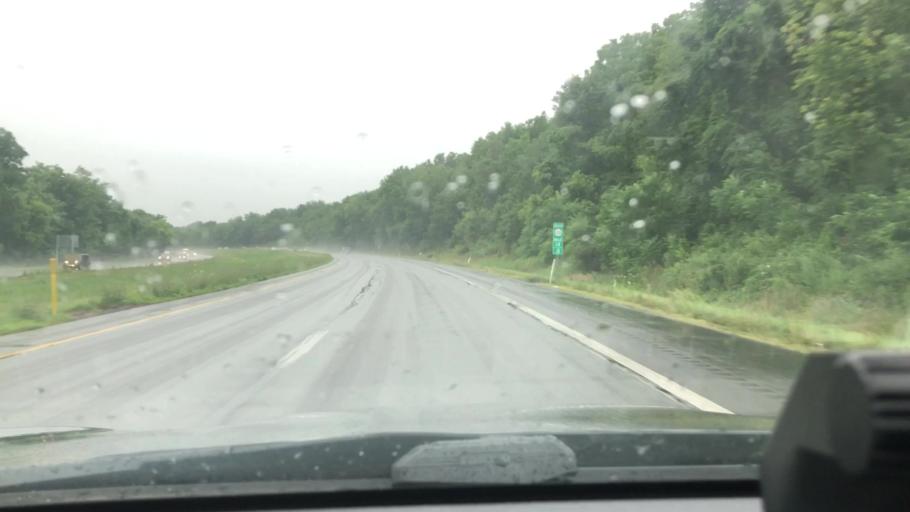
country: US
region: Pennsylvania
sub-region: Northampton County
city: Wind Gap
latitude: 40.8137
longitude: -75.3008
